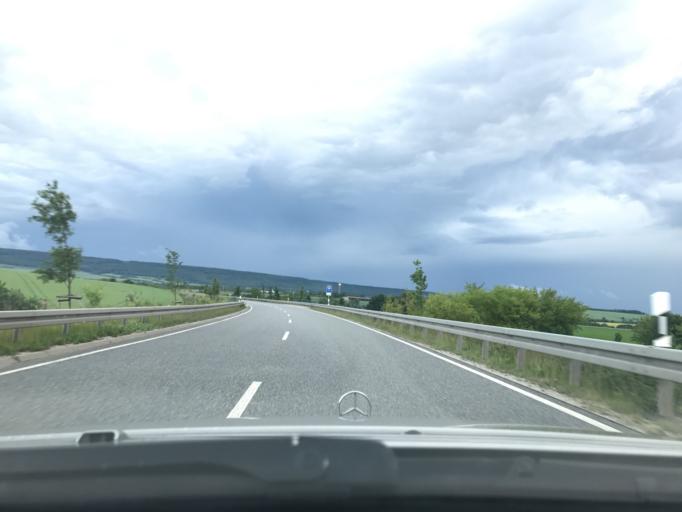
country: DE
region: Thuringia
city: Breitenworbis
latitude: 51.3954
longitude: 10.4267
